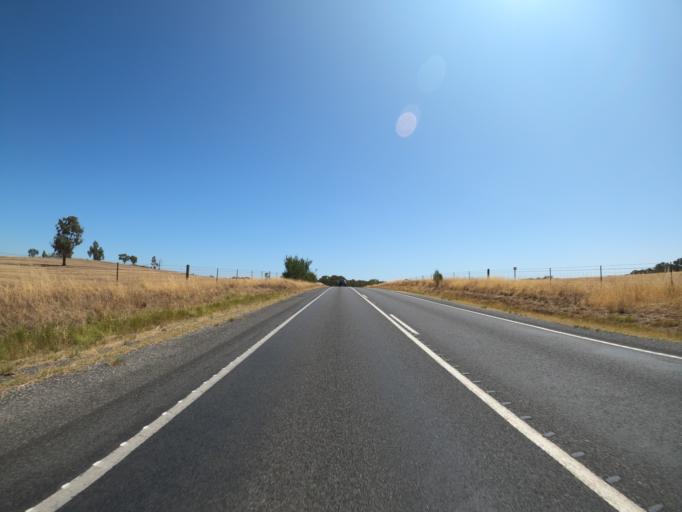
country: AU
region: New South Wales
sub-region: Corowa Shire
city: Corowa
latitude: -36.0559
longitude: 146.4421
